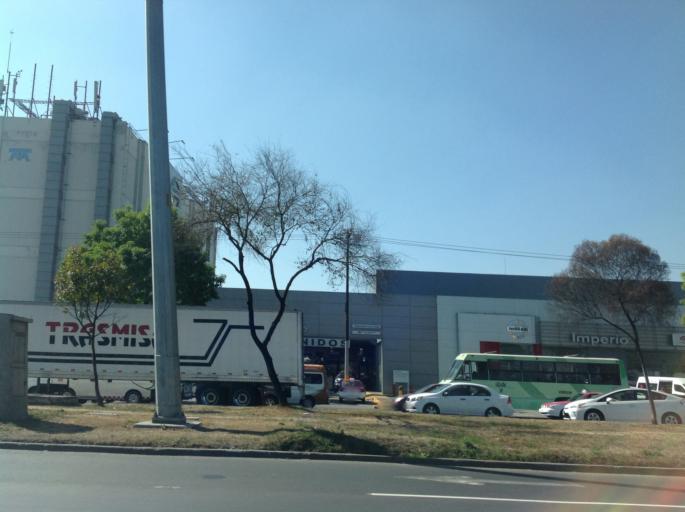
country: MX
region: Mexico
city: Ciudad Nezahualcoyotl
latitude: 19.3868
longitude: -99.0391
